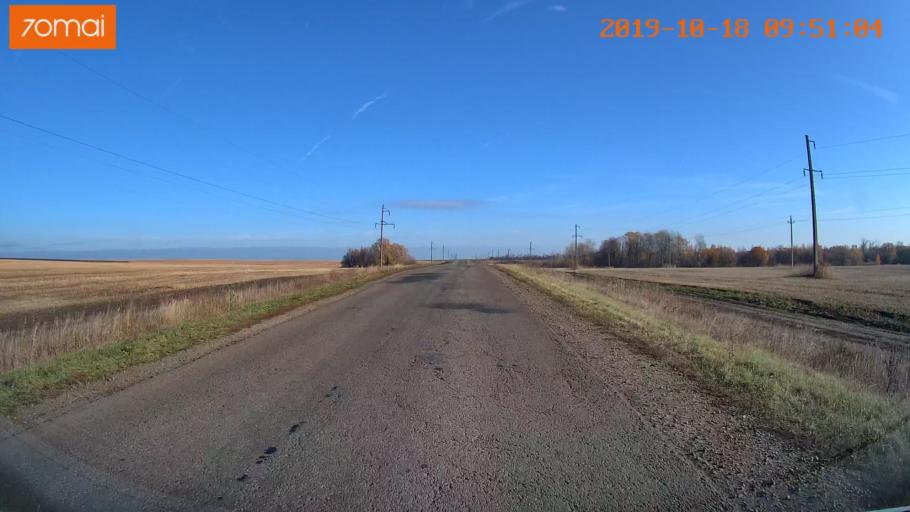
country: RU
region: Tula
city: Kazachka
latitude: 53.3360
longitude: 38.2863
